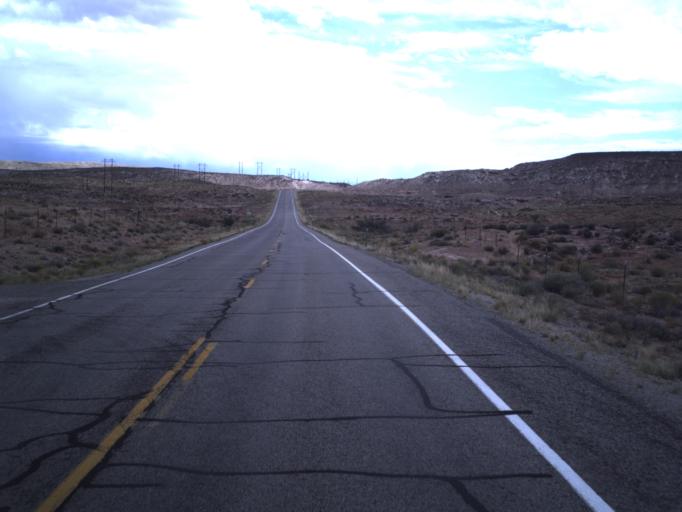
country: US
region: Utah
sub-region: San Juan County
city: Blanding
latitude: 37.2878
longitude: -109.3949
